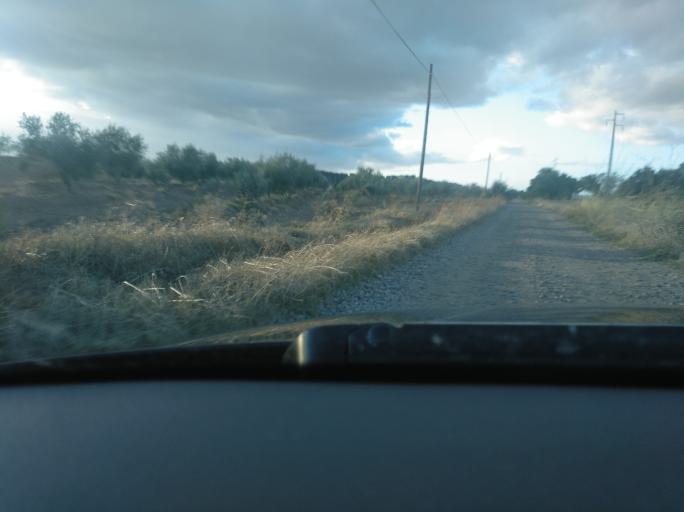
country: PT
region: Portalegre
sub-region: Campo Maior
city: Campo Maior
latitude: 39.0388
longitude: -6.9897
